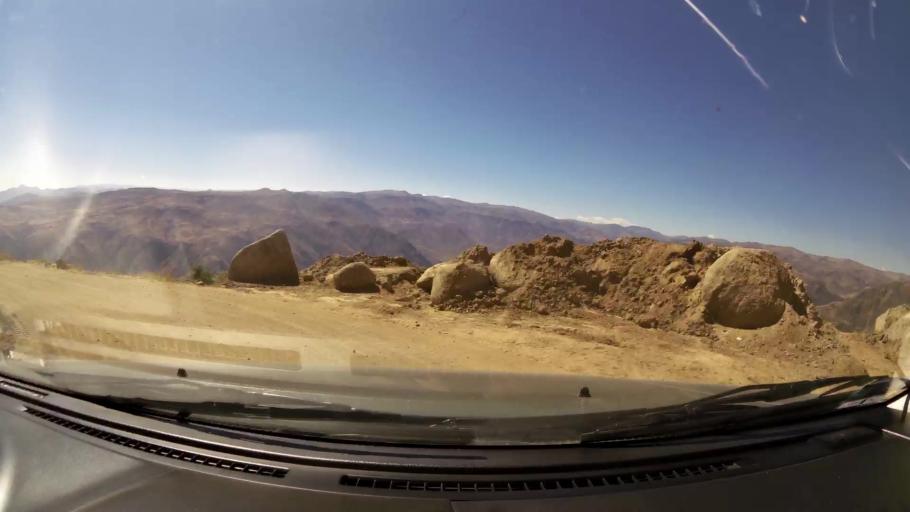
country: PE
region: Huancavelica
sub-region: Huaytara
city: Quito-Arma
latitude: -13.6247
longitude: -75.3486
